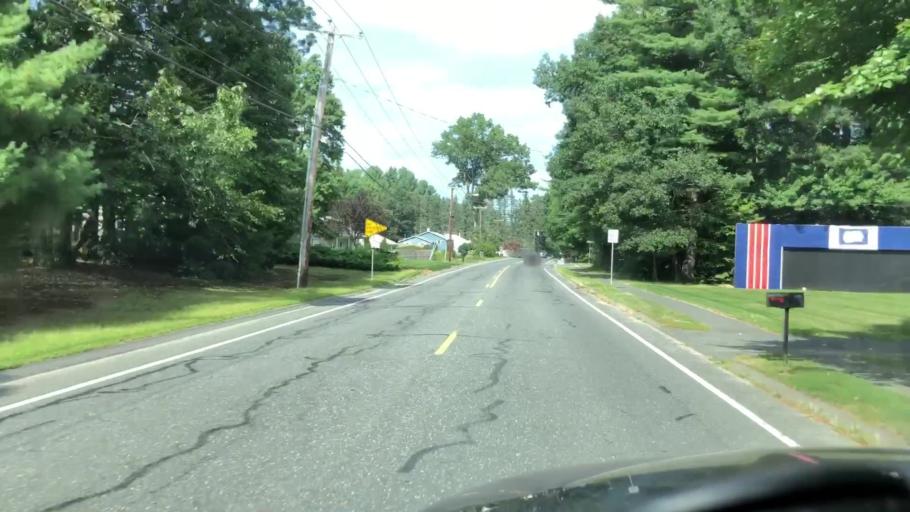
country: US
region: Massachusetts
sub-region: Hampshire County
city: Southampton
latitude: 42.2494
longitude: -72.7228
